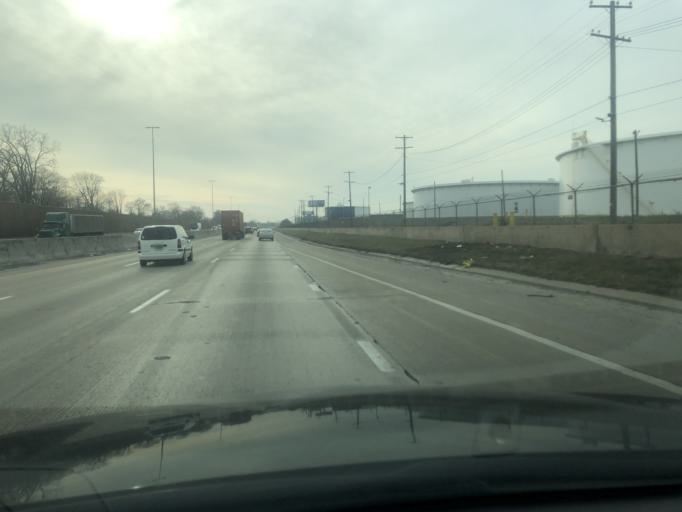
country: US
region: Michigan
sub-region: Wayne County
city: Melvindale
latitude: 42.2747
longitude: -83.1619
